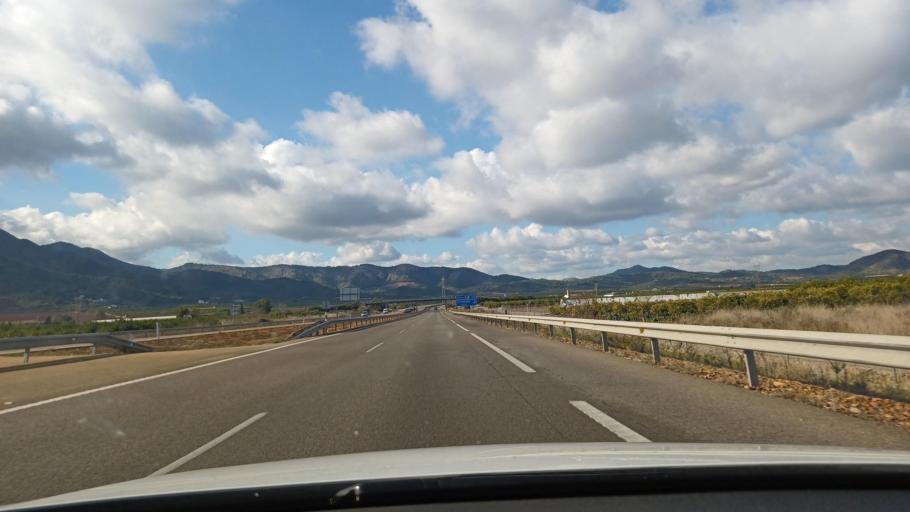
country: ES
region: Valencia
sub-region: Provincia de Castello
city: Villavieja
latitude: 39.8668
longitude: -0.1758
